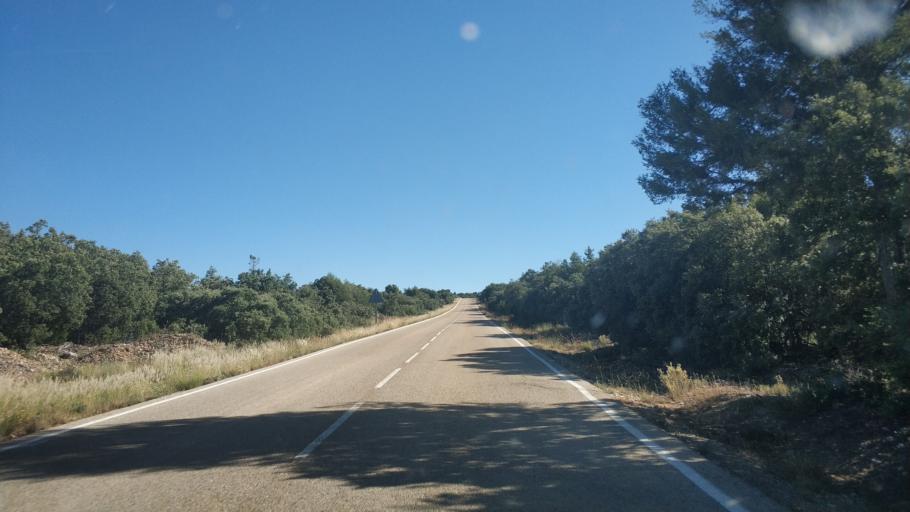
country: ES
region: Castille and Leon
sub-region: Provincia de Soria
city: Montejo de Tiermes
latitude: 41.4093
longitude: -3.2014
